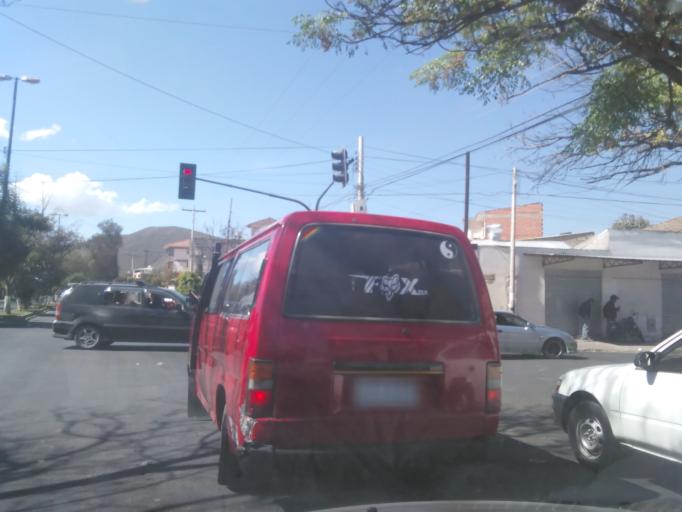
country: BO
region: Cochabamba
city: Cochabamba
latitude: -17.3983
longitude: -66.1476
